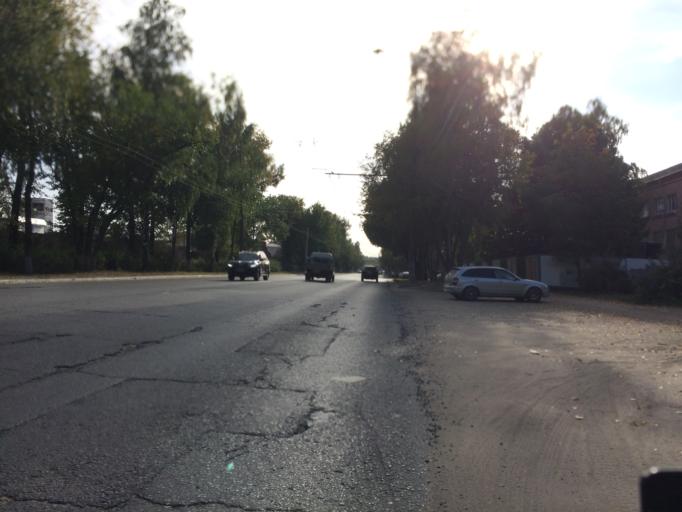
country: RU
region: Mariy-El
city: Medvedevo
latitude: 56.6282
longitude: 47.8439
